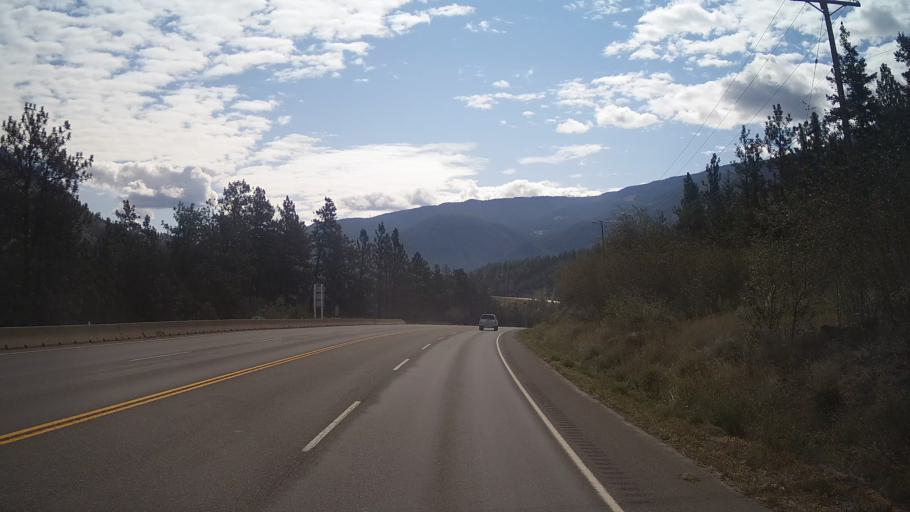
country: CA
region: British Columbia
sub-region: Thompson-Nicola Regional District
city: Ashcroft
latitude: 50.2583
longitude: -121.5283
